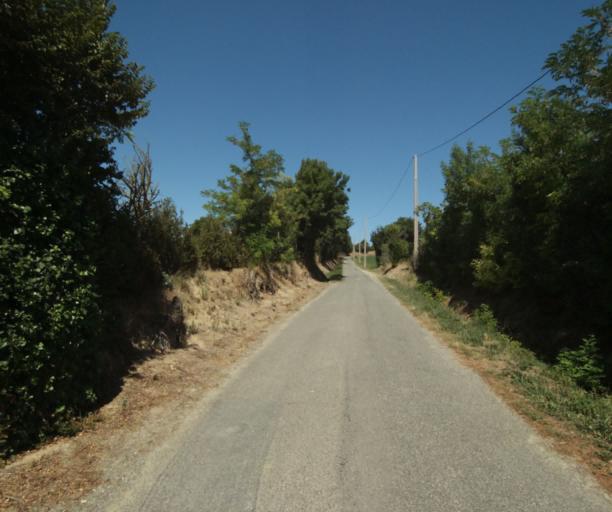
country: FR
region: Midi-Pyrenees
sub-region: Departement de la Haute-Garonne
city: Saint-Felix-Lauragais
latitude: 43.4906
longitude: 1.9285
